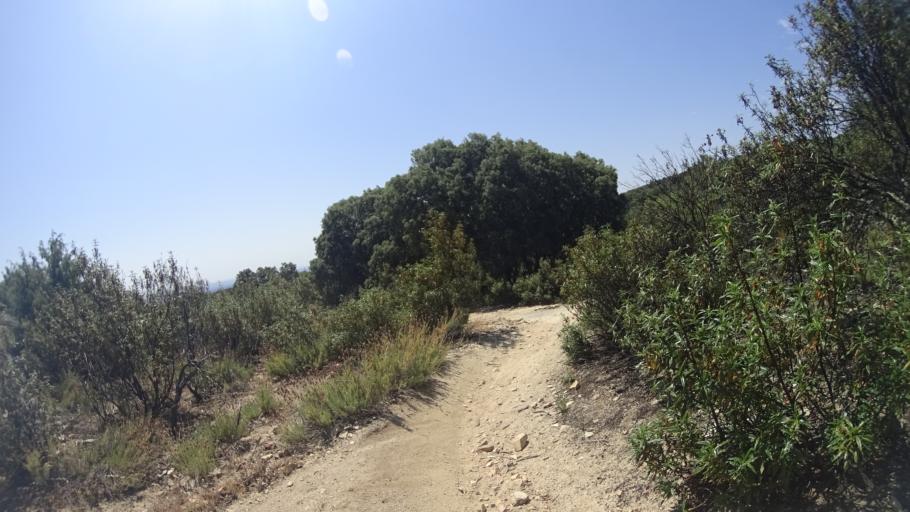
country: ES
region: Madrid
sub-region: Provincia de Madrid
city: Torrelodones
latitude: 40.5972
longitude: -3.9255
